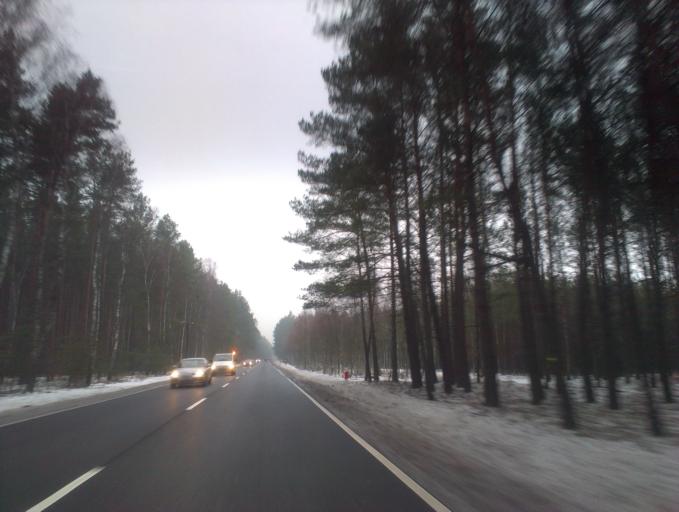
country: PL
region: Greater Poland Voivodeship
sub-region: Powiat zlotowski
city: Tarnowka
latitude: 53.2841
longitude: 16.7824
